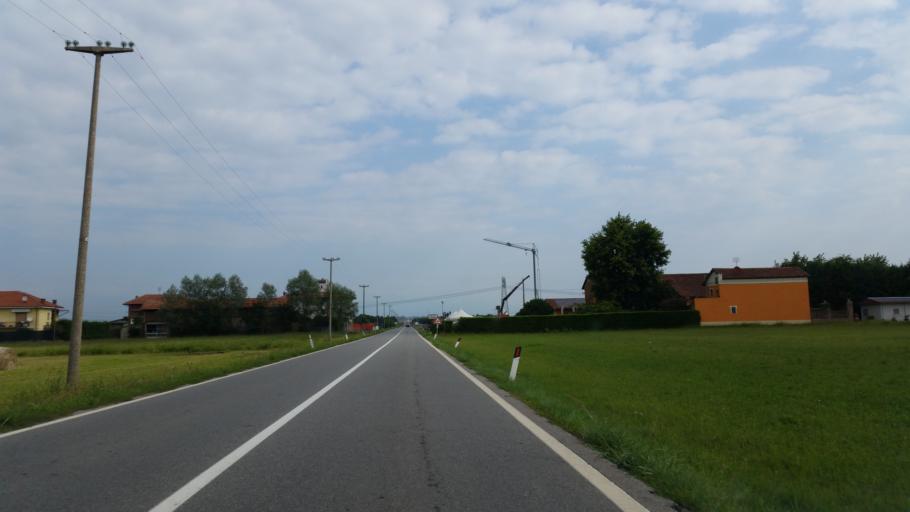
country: IT
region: Piedmont
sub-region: Provincia di Torino
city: Montanaro
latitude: 45.2542
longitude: 7.8918
